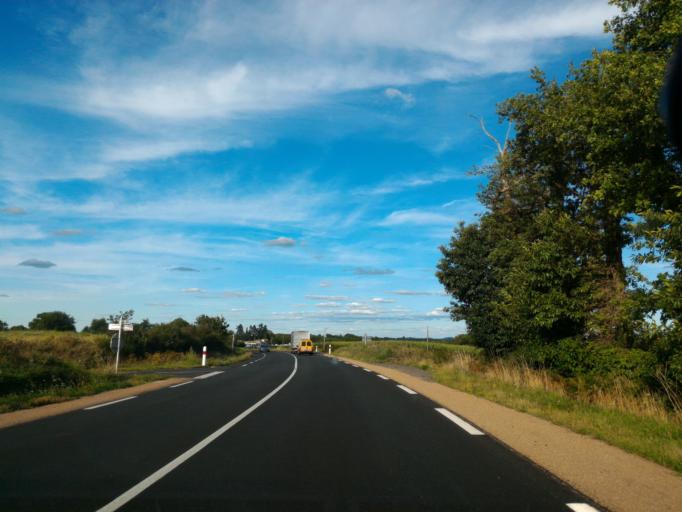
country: FR
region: Limousin
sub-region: Departement de la Haute-Vienne
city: Magnac-Laval
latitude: 46.1890
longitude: 1.2312
